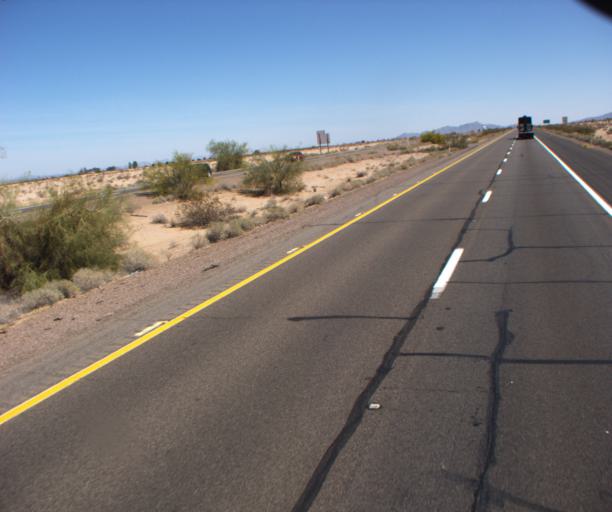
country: US
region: Arizona
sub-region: Yuma County
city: Wellton
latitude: 32.6838
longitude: -114.0106
